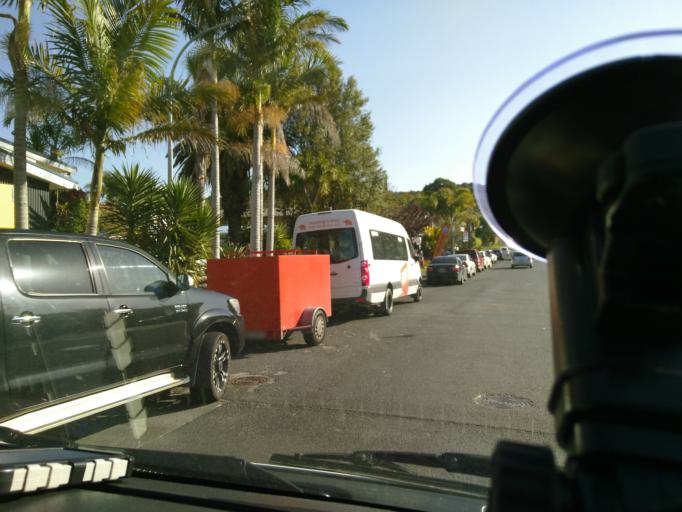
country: NZ
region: Northland
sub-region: Far North District
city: Paihia
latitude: -35.2854
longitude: 174.0949
